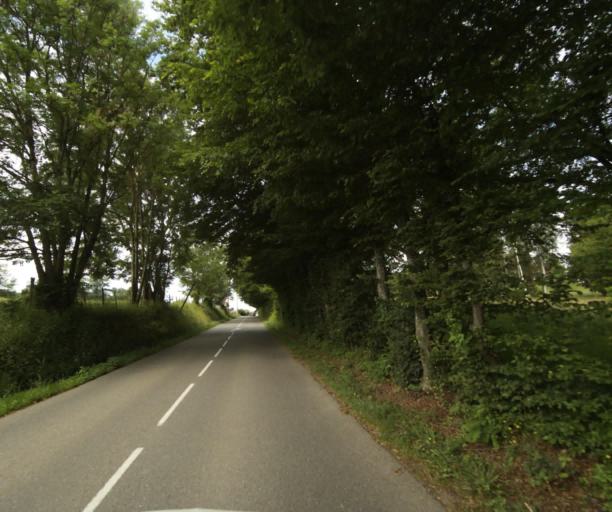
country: FR
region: Rhone-Alpes
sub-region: Departement de la Haute-Savoie
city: Margencel
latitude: 46.3301
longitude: 6.4257
